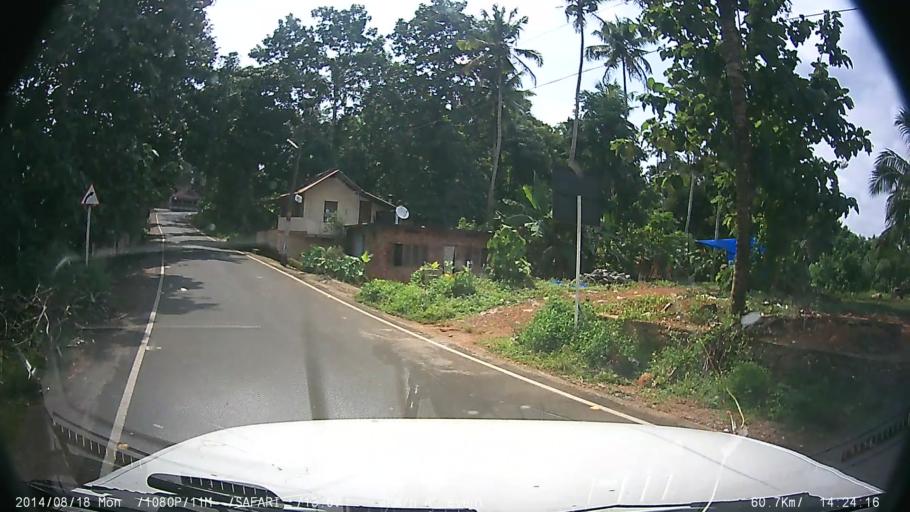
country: IN
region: Kerala
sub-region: Ernakulam
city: Piravam
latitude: 9.7926
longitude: 76.5258
